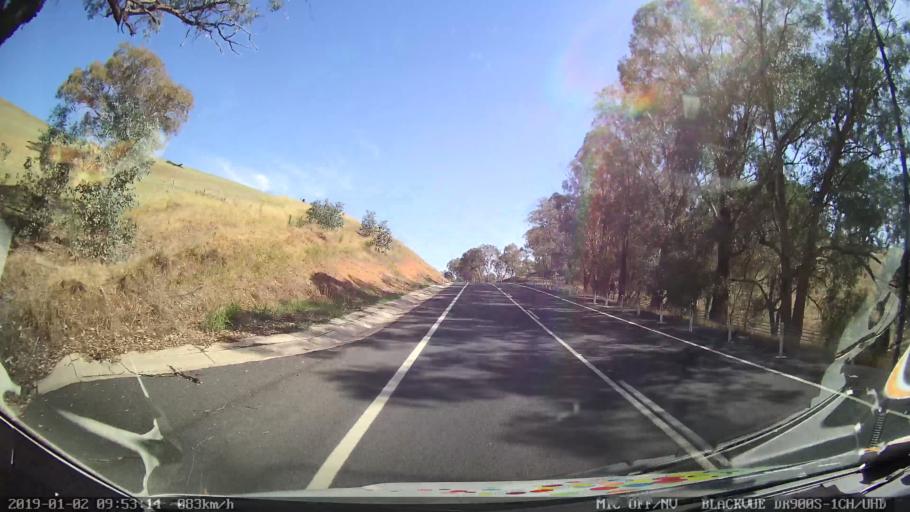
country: AU
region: New South Wales
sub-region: Tumut Shire
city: Tumut
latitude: -35.2503
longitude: 148.2035
